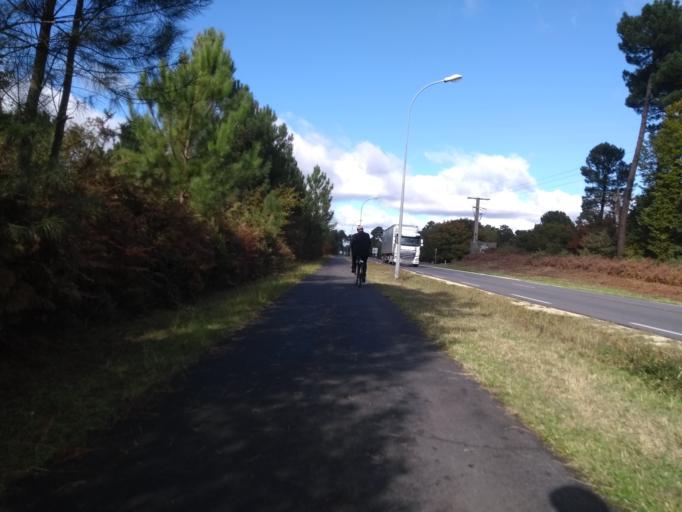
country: FR
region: Aquitaine
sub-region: Departement de la Gironde
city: Cestas
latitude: 44.7656
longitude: -0.6902
